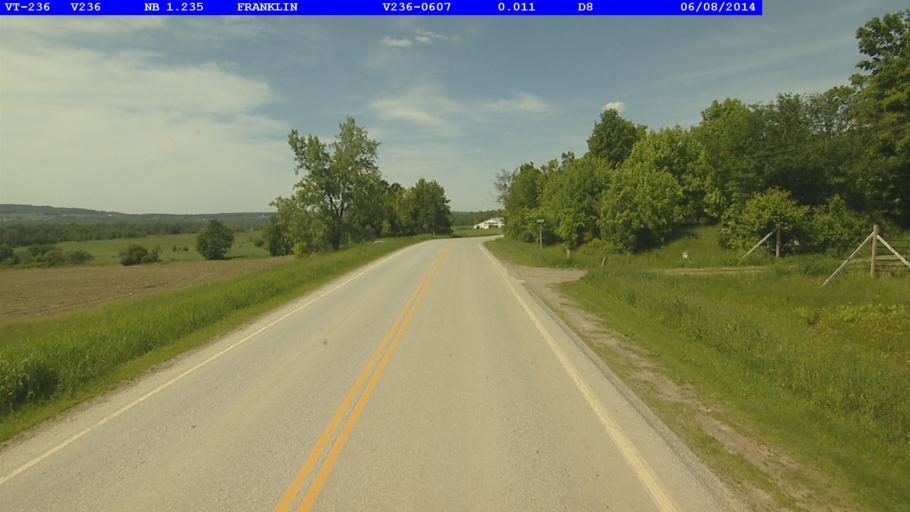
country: US
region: Vermont
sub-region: Franklin County
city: Enosburg Falls
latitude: 44.9286
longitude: -72.8659
